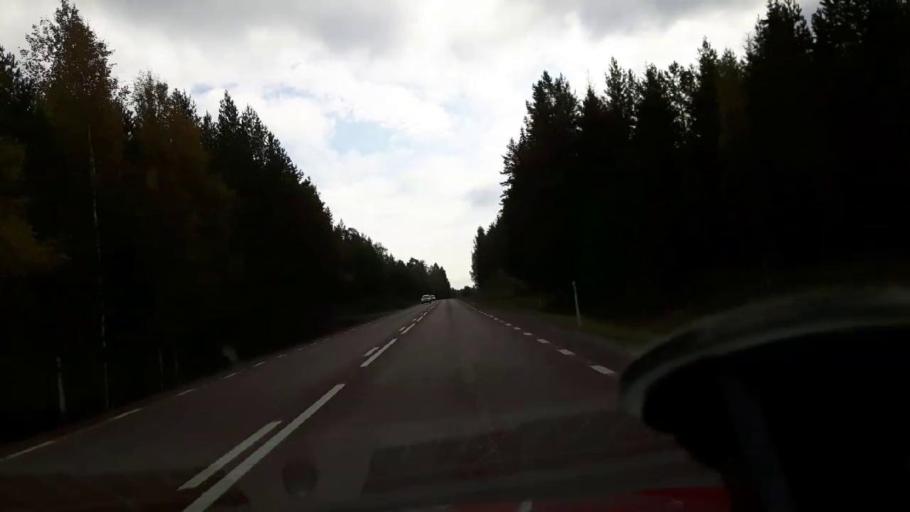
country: SE
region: Gaevleborg
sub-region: Bollnas Kommun
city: Kilafors
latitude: 61.2658
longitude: 16.5470
